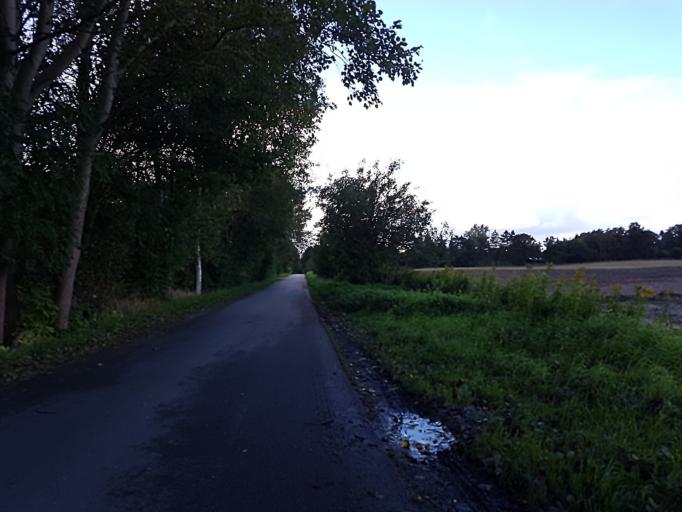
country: DK
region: Capital Region
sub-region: Egedal Kommune
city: Vekso
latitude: 55.7362
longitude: 12.2101
